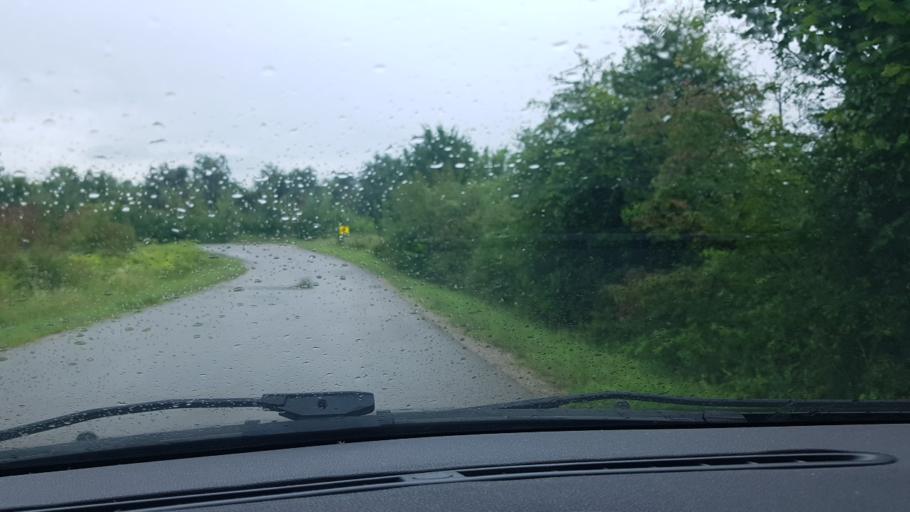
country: BA
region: Federation of Bosnia and Herzegovina
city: Trzacka Rastela
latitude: 44.9763
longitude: 15.7104
